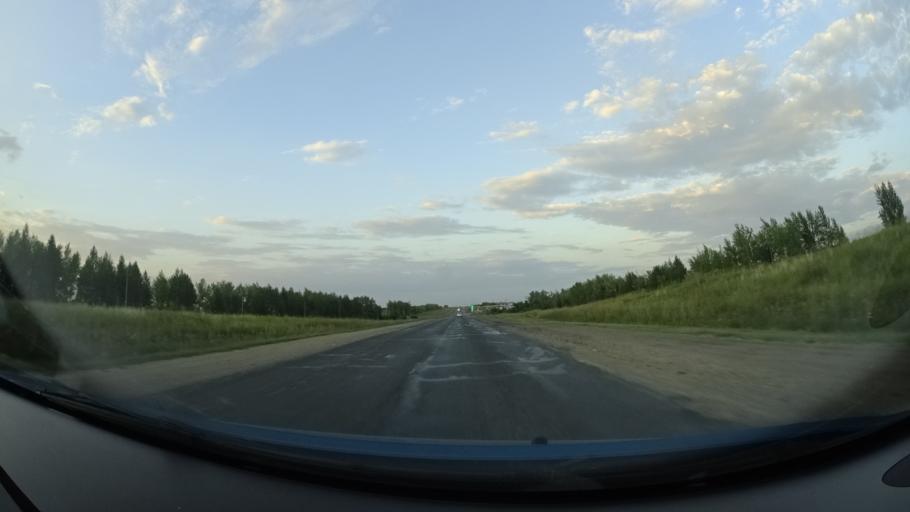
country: RU
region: Orenburg
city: Severnoye
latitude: 54.2169
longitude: 52.7234
